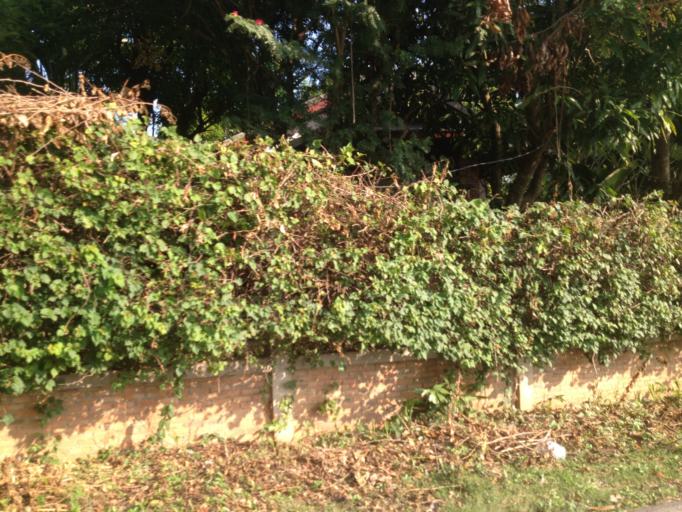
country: TH
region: Chiang Mai
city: Hang Dong
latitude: 18.7183
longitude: 98.9314
